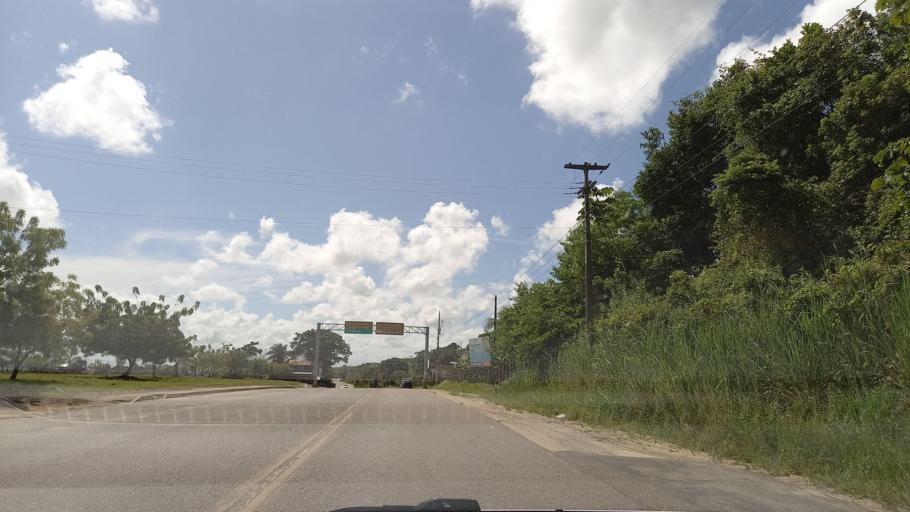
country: BR
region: Pernambuco
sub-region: Barreiros
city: Barreiros
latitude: -8.8071
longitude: -35.1852
